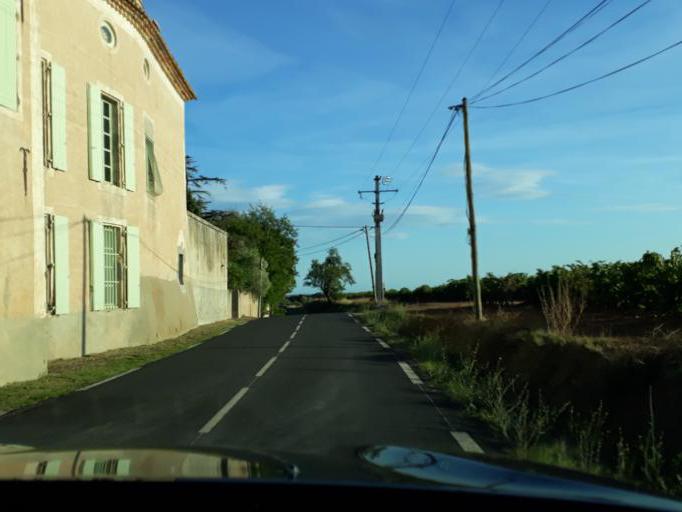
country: FR
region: Languedoc-Roussillon
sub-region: Departement de l'Herault
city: Pomerols
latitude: 43.4013
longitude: 3.4933
